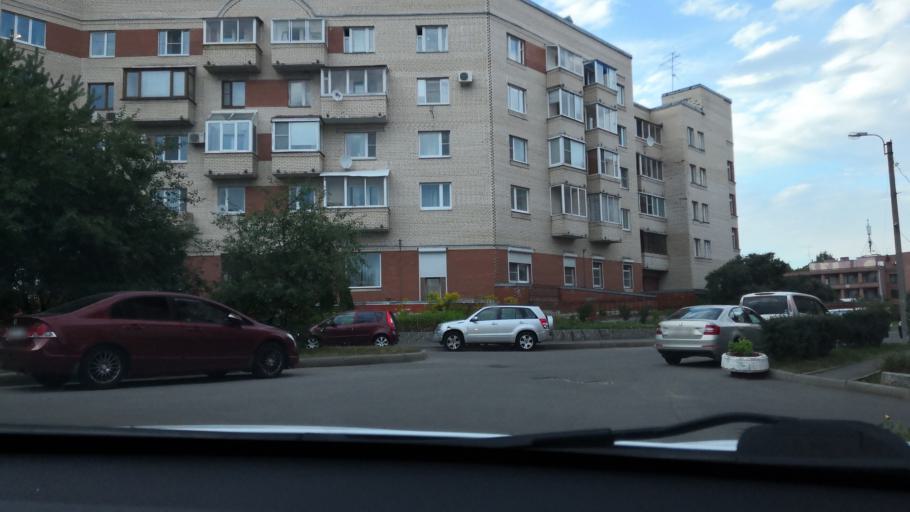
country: RU
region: St.-Petersburg
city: Pavlovsk
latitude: 59.6944
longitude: 30.4231
